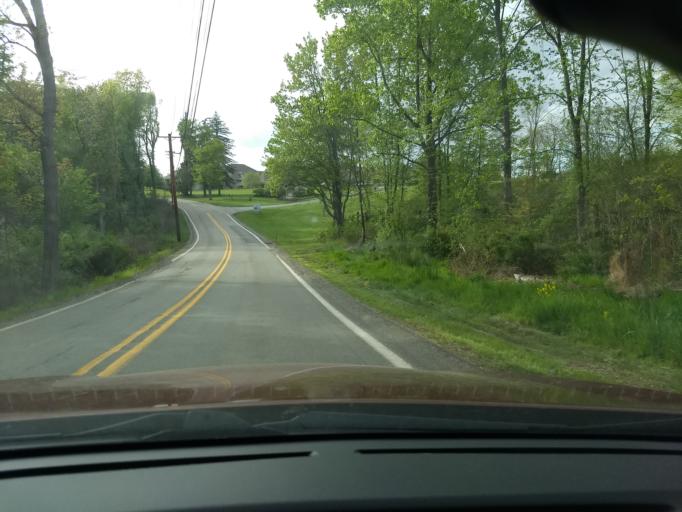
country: US
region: Pennsylvania
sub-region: Allegheny County
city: Russellton
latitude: 40.6007
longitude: -79.8959
